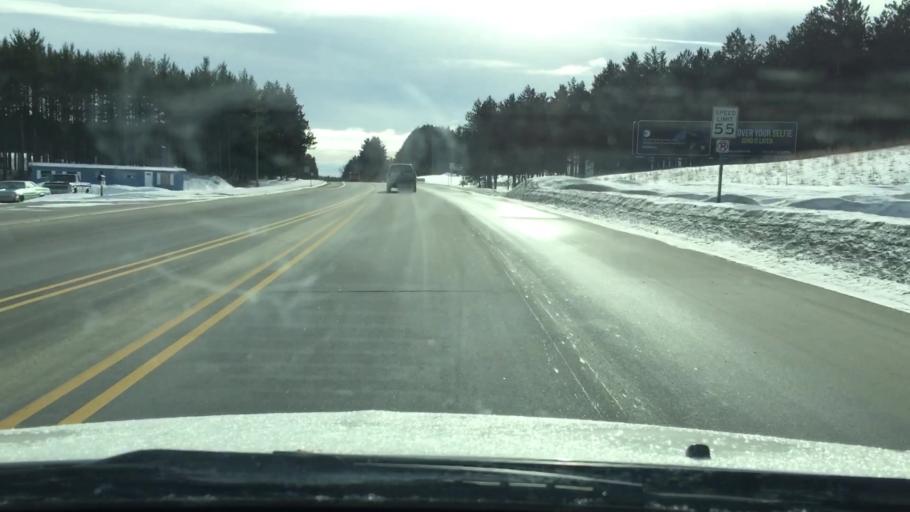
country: US
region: Michigan
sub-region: Kalkaska County
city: Kalkaska
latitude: 44.6402
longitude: -85.2871
